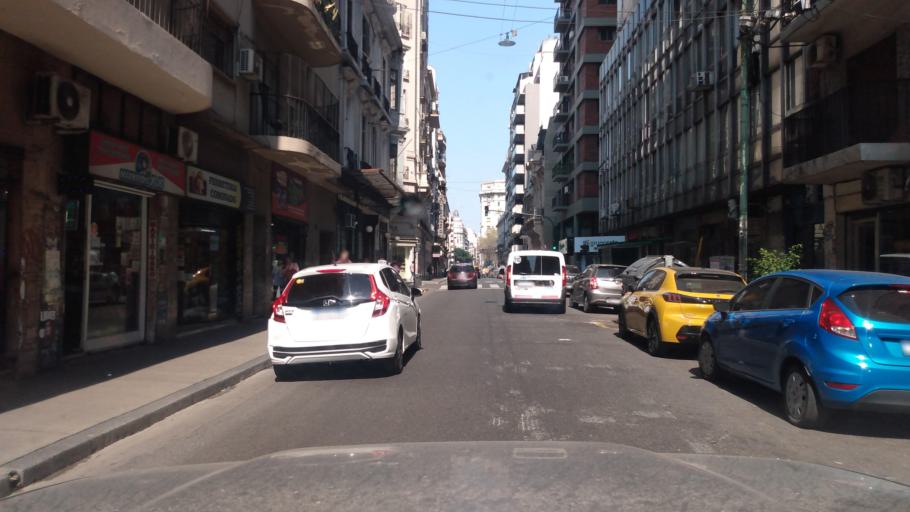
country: AR
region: Buenos Aires F.D.
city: Buenos Aires
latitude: -34.6075
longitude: -58.3907
